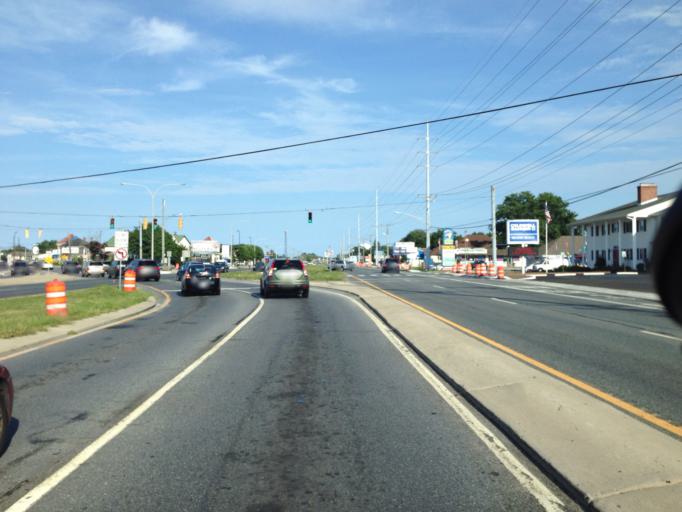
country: US
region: Delaware
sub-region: Sussex County
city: Rehoboth Beach
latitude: 38.7128
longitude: -75.1028
